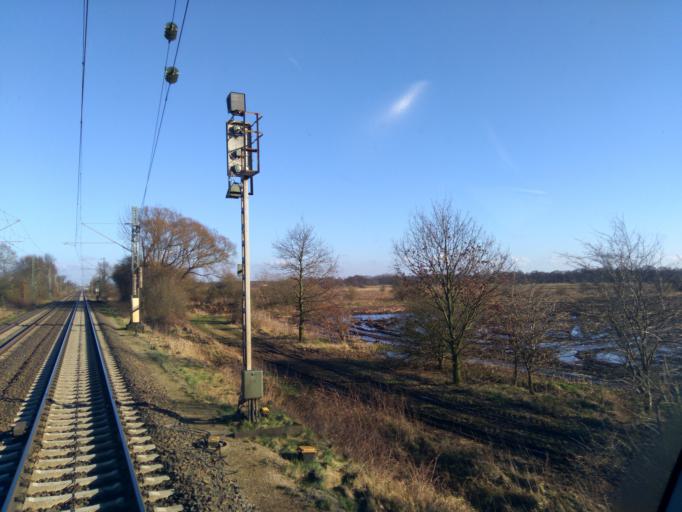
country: DE
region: Lower Saxony
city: Oyten
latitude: 53.0872
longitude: 9.0440
